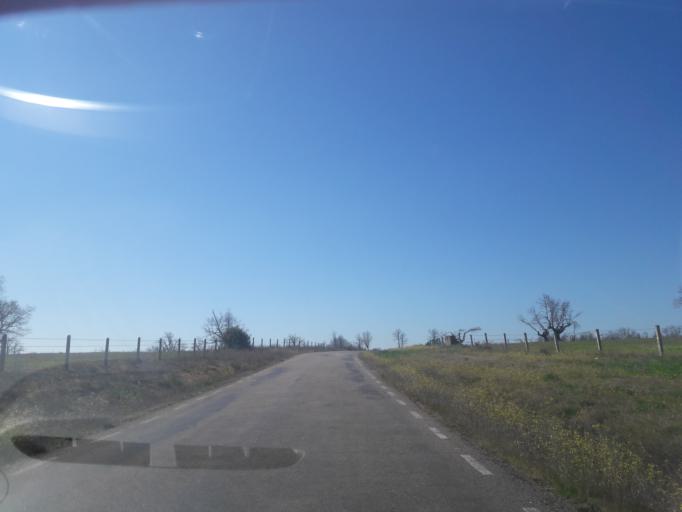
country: ES
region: Castille and Leon
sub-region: Provincia de Salamanca
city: Valsalabroso
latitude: 41.1355
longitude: -6.4828
